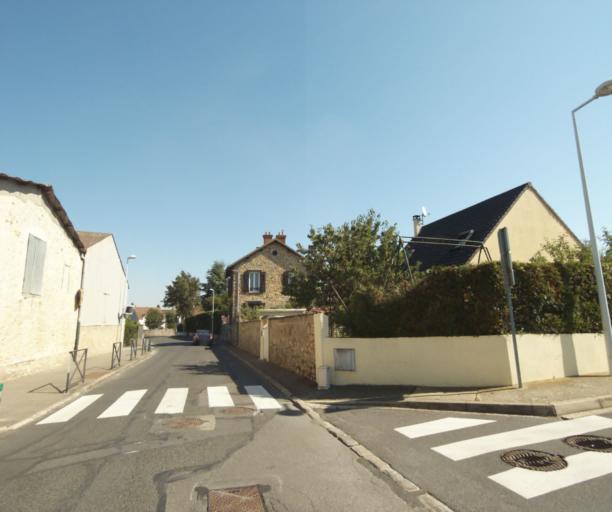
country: FR
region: Ile-de-France
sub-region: Departement de Seine-et-Marne
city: Moissy-Cramayel
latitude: 48.6258
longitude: 2.5954
